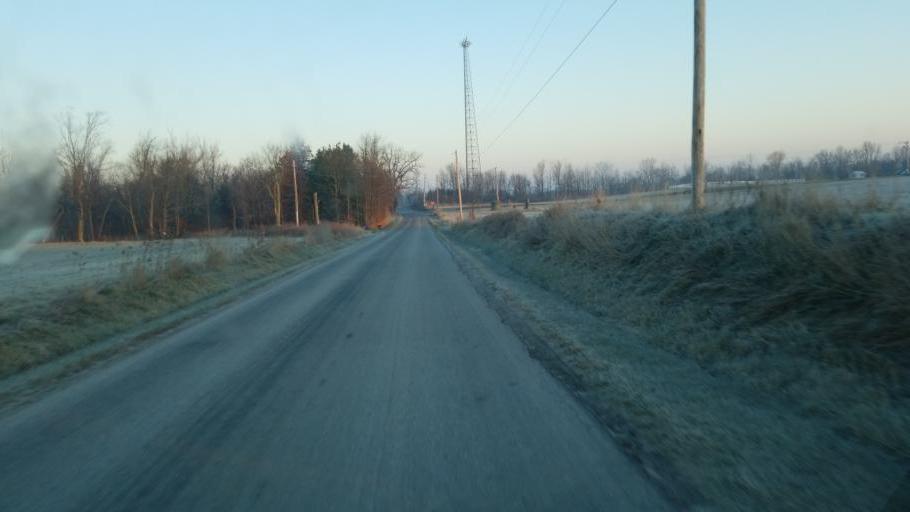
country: US
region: Ohio
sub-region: Wayne County
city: West Salem
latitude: 40.9847
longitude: -82.0545
